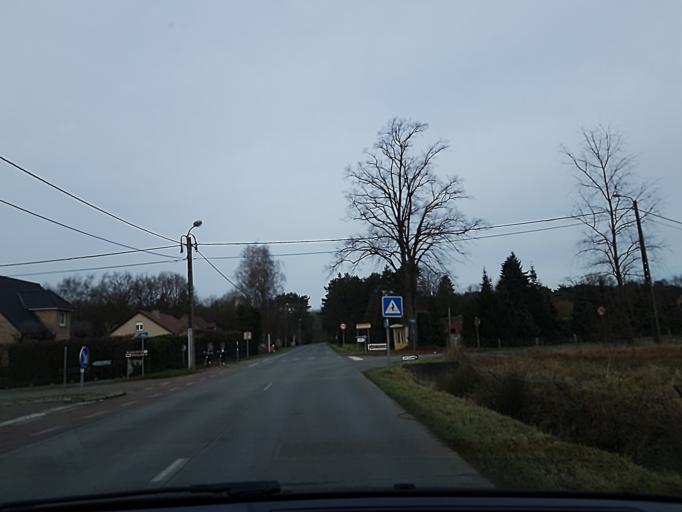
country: BE
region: Flanders
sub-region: Provincie Vlaams-Brabant
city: Keerbergen
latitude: 51.0134
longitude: 4.6002
